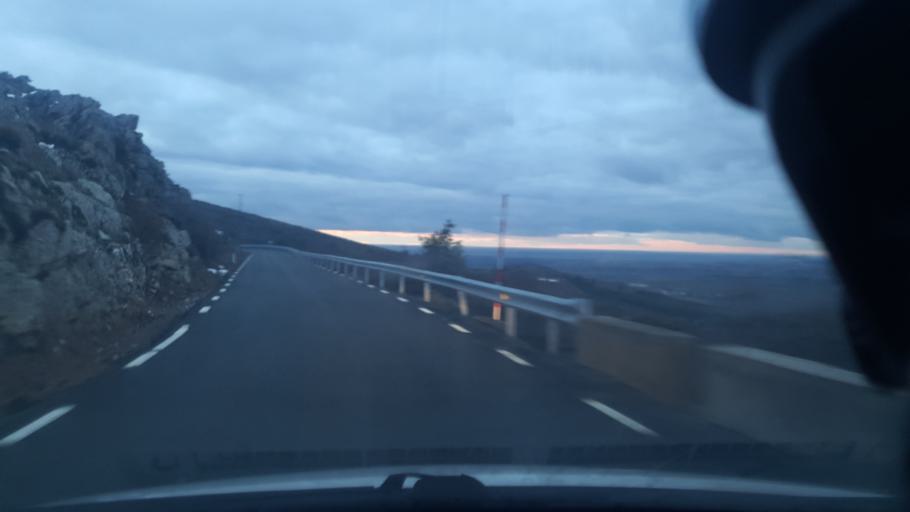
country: ES
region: Castille and Leon
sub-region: Provincia de Avila
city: Ojos-Albos
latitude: 40.7212
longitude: -4.4516
